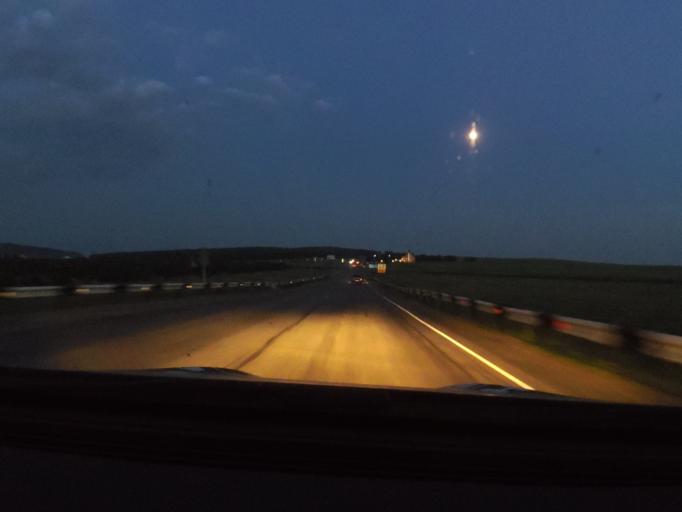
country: RU
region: Bashkortostan
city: Duvan
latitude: 55.9214
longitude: 58.2070
